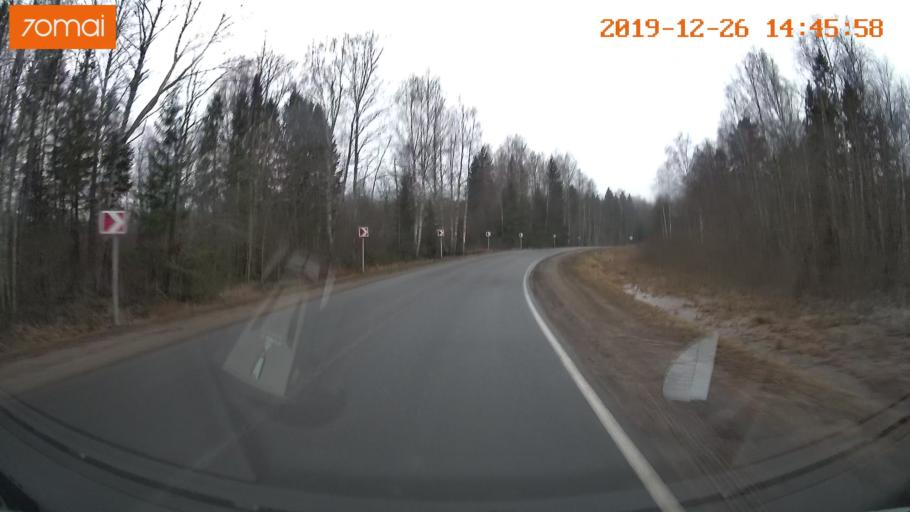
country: RU
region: Jaroslavl
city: Poshekhon'ye
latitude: 58.3348
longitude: 39.0273
